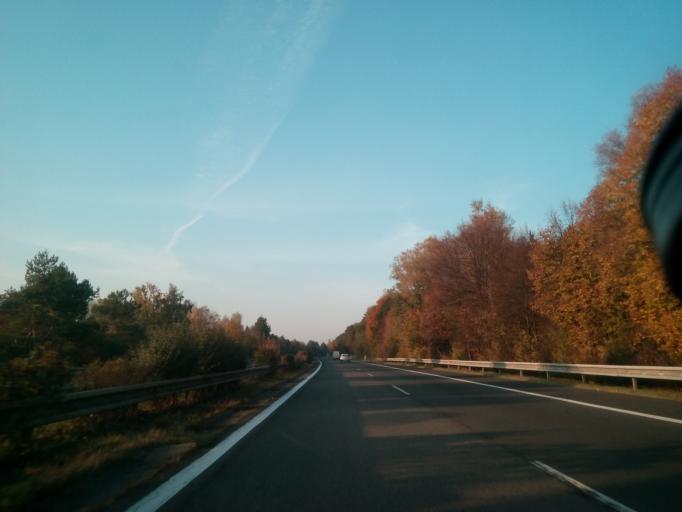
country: SK
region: Presovsky
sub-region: Okres Presov
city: Presov
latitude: 48.9448
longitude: 21.2576
